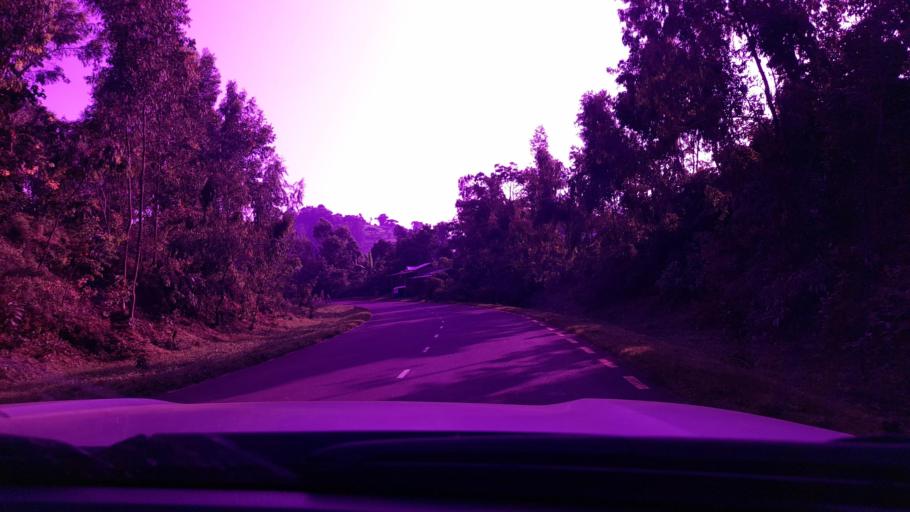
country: ET
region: Oromiya
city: Bedele
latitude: 8.1408
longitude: 36.4581
